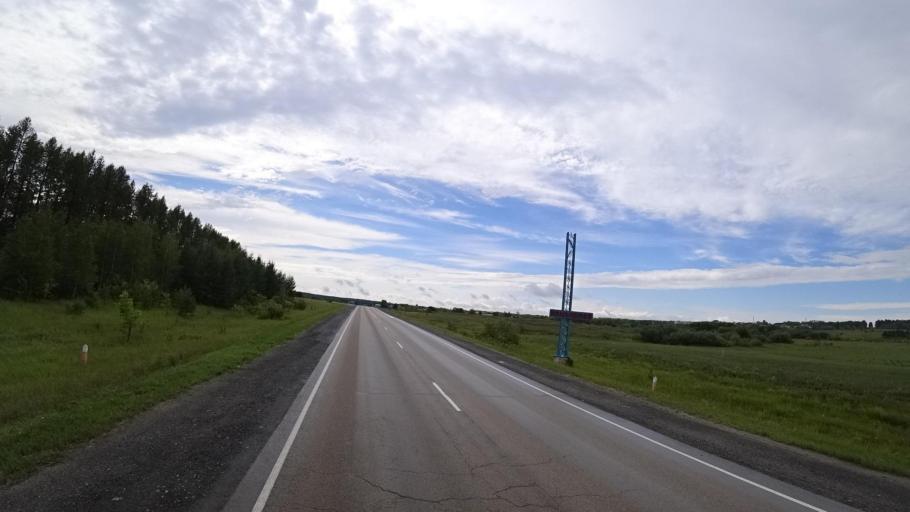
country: RU
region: Sverdlovsk
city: Kamyshlov
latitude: 56.8431
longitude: 62.8052
